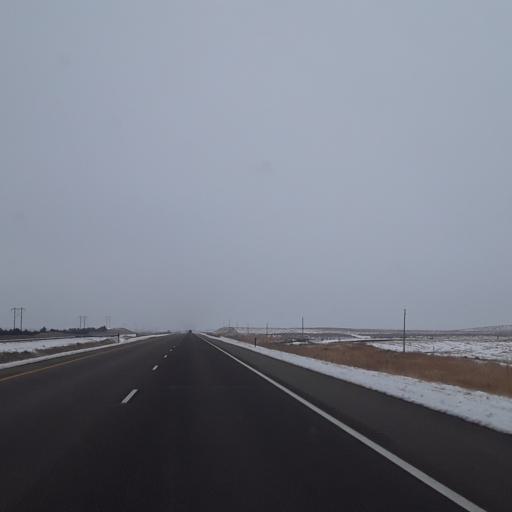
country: US
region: Colorado
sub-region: Logan County
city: Sterling
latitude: 40.4749
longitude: -103.2843
